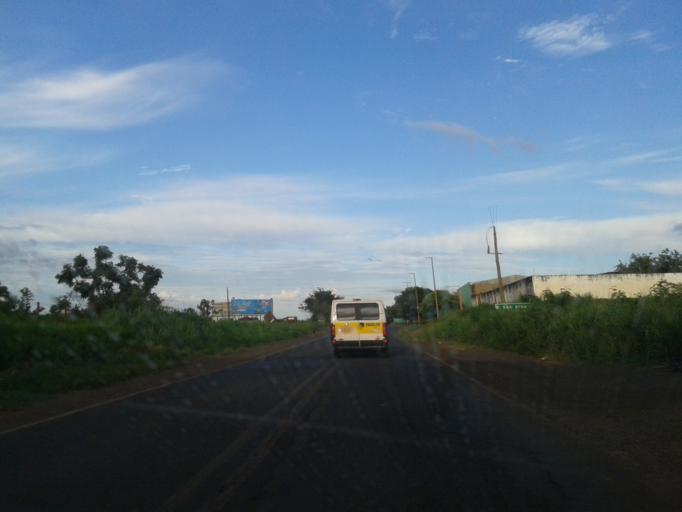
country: BR
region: Minas Gerais
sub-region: Araguari
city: Araguari
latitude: -18.6416
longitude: -48.2173
